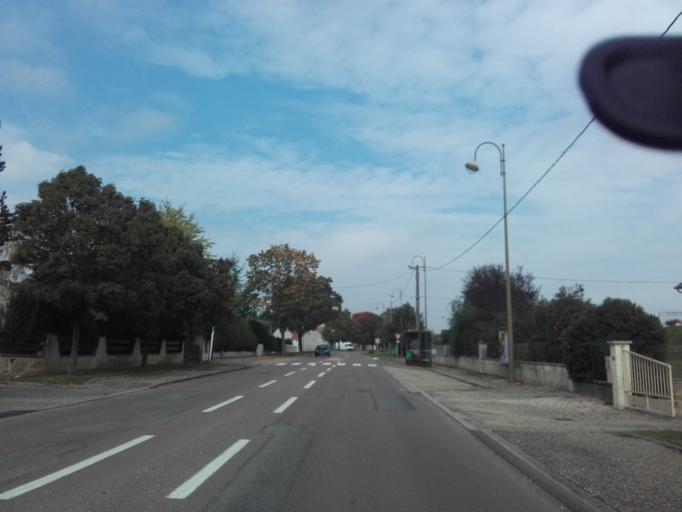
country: FR
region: Bourgogne
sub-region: Departement de la Cote-d'Or
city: Bligny-les-Beaune
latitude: 46.9811
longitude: 4.8213
